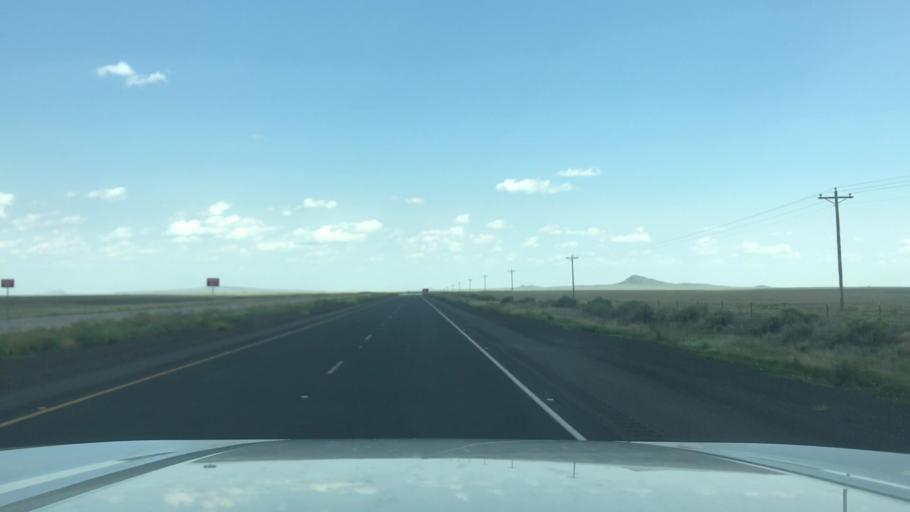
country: US
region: New Mexico
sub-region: Union County
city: Clayton
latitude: 36.6322
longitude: -103.7154
